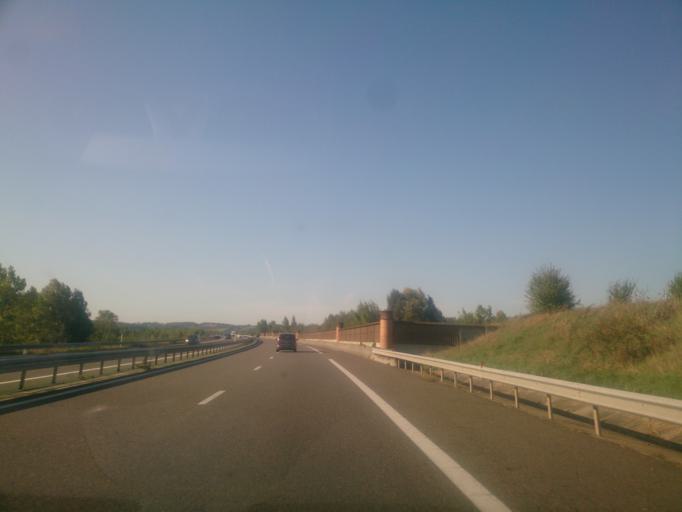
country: FR
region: Midi-Pyrenees
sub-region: Departement du Tarn-et-Garonne
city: Albias
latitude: 44.0670
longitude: 1.4231
